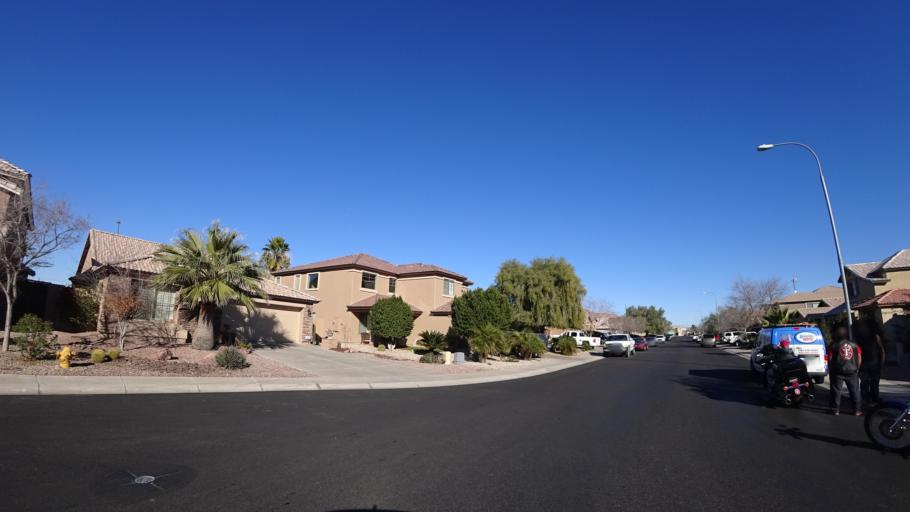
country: US
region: Arizona
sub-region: Maricopa County
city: Avondale
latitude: 33.4348
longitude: -112.3144
